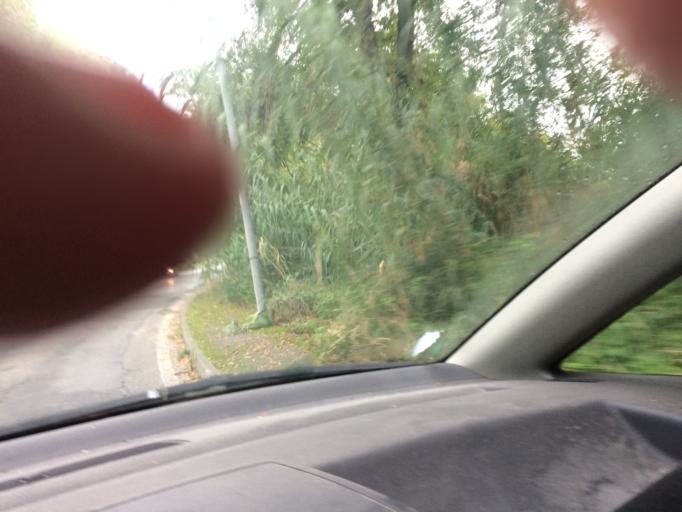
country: IT
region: Tuscany
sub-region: Provincia di Massa-Carrara
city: Massa
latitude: 44.0291
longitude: 10.0941
